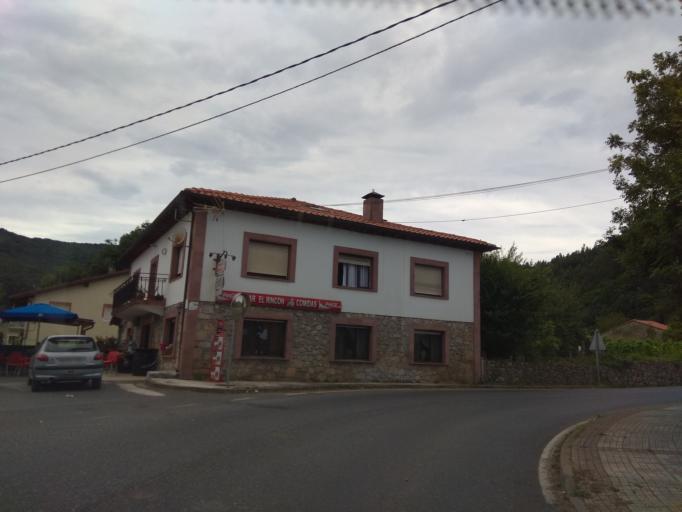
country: ES
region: Cantabria
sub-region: Provincia de Cantabria
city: Hazas de Cesto
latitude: 43.3990
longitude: -3.5978
